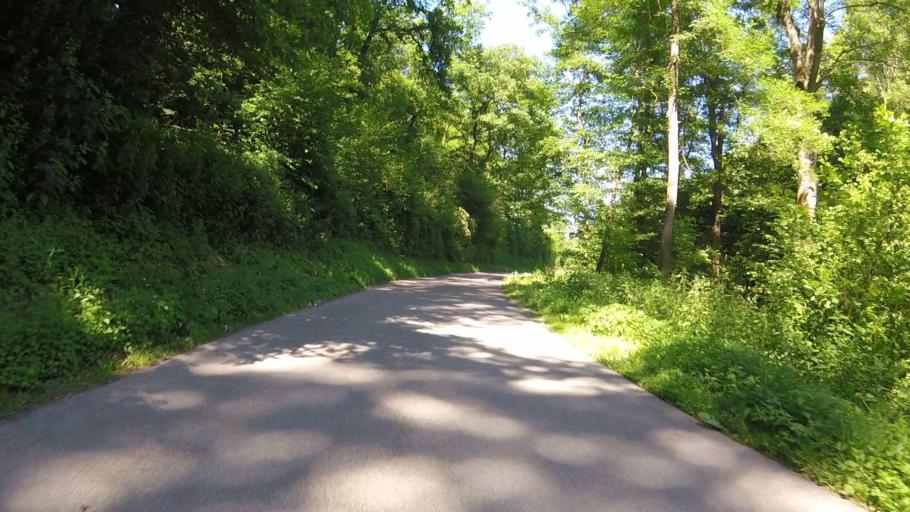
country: DE
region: Baden-Wuerttemberg
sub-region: Regierungsbezirk Stuttgart
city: Steinheim am der Murr
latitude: 48.9667
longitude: 9.3013
